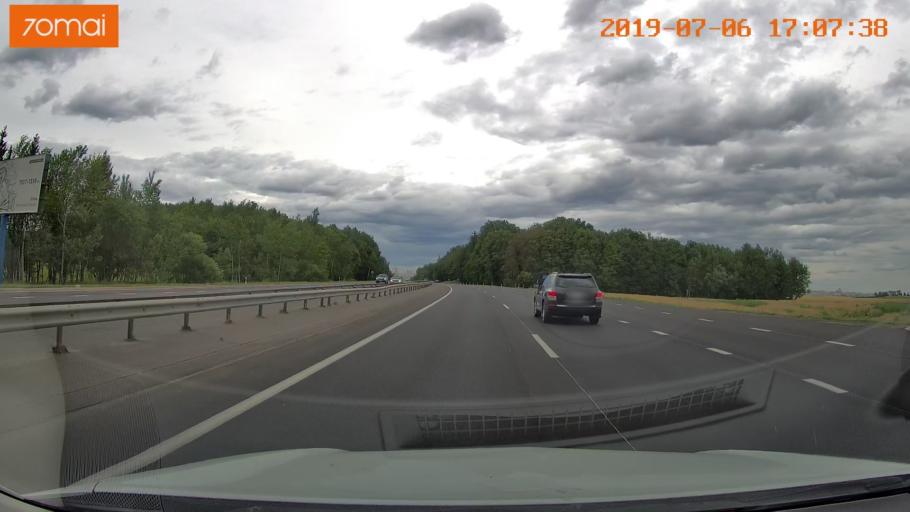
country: BY
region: Minsk
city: Khatsyezhyna
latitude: 53.9073
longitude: 27.3694
